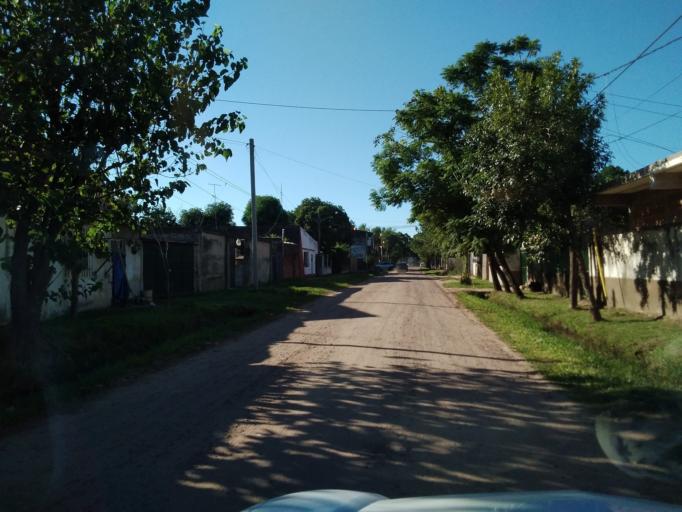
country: AR
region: Corrientes
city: Corrientes
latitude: -27.4705
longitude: -58.7961
